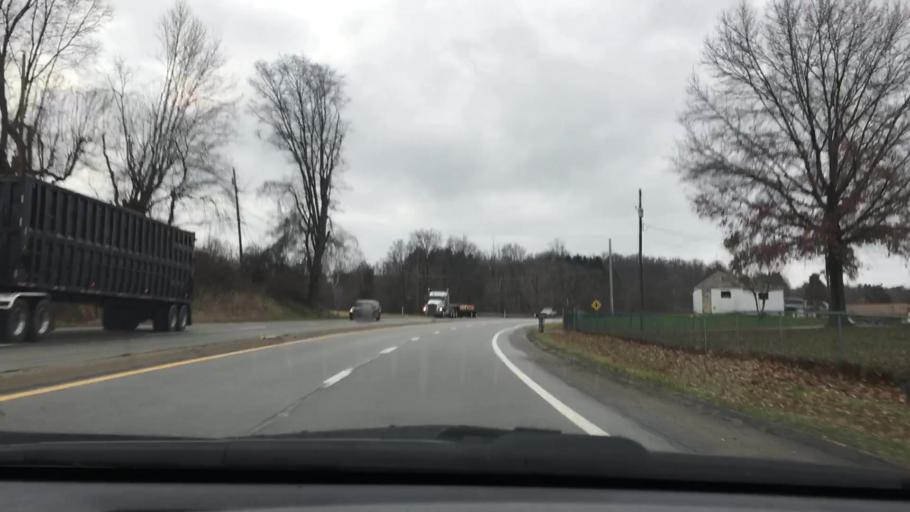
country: US
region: Pennsylvania
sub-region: Westmoreland County
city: West Newton
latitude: 40.1485
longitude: -79.7722
